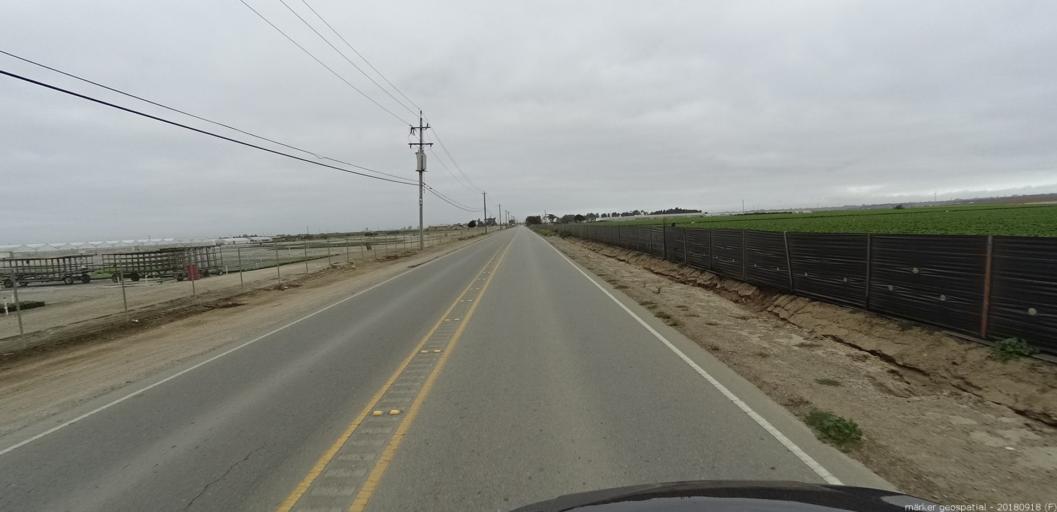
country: US
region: California
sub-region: Monterey County
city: Prunedale
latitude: 36.7403
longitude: -121.6775
